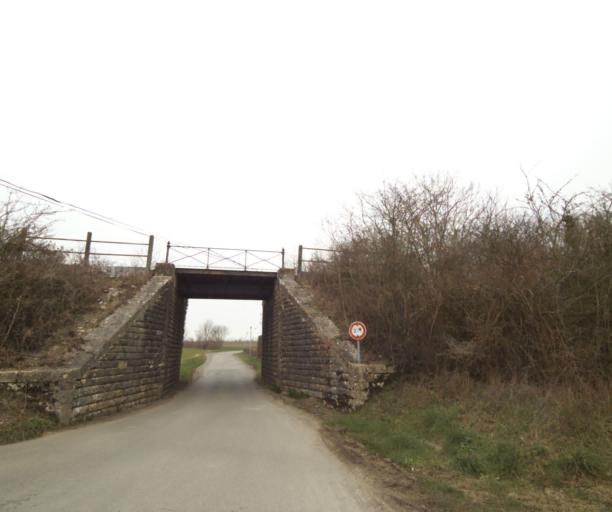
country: FR
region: Poitou-Charentes
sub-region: Departement des Deux-Sevres
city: Magne
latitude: 46.3310
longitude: -0.5295
